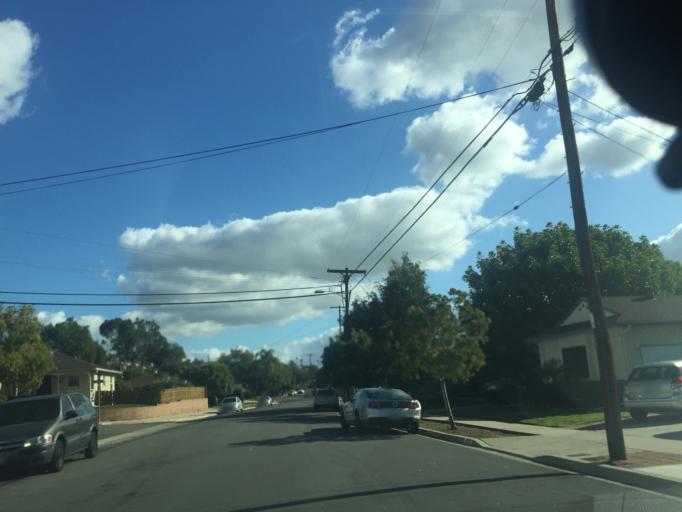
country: US
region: California
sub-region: San Diego County
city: La Mesa
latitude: 32.7840
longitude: -117.0920
